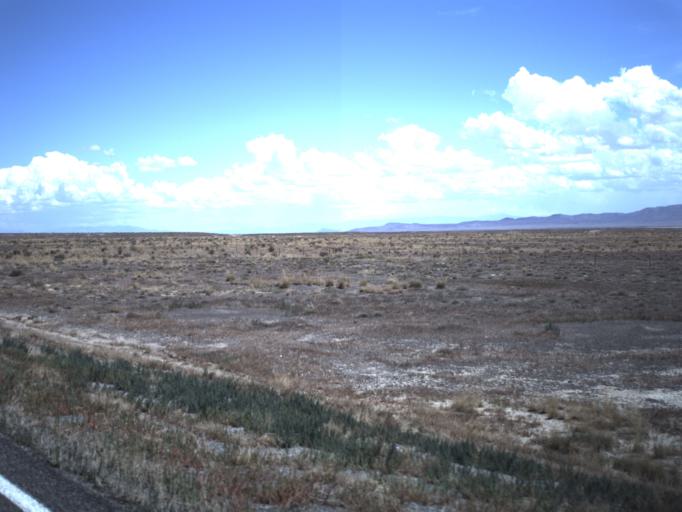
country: US
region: Utah
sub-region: Millard County
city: Delta
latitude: 39.1254
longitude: -113.1117
